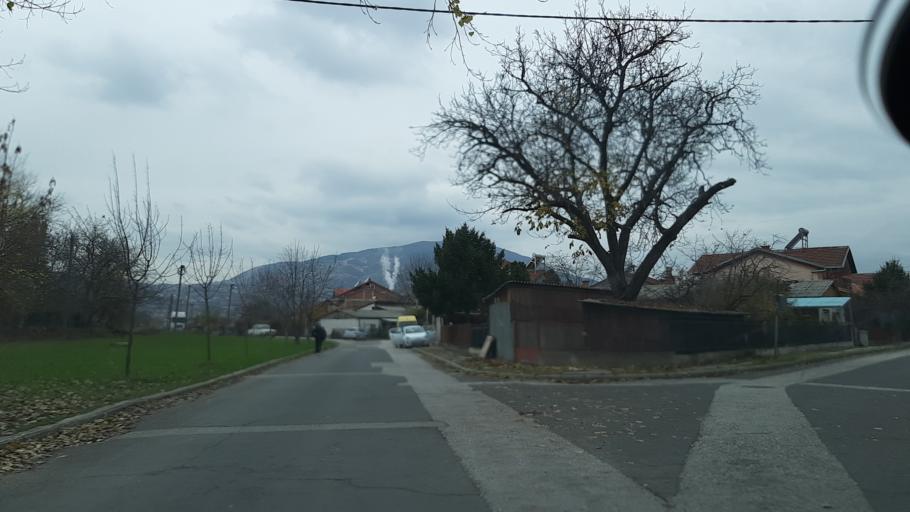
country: MK
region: Kisela Voda
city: Usje
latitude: 41.9709
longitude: 21.4760
